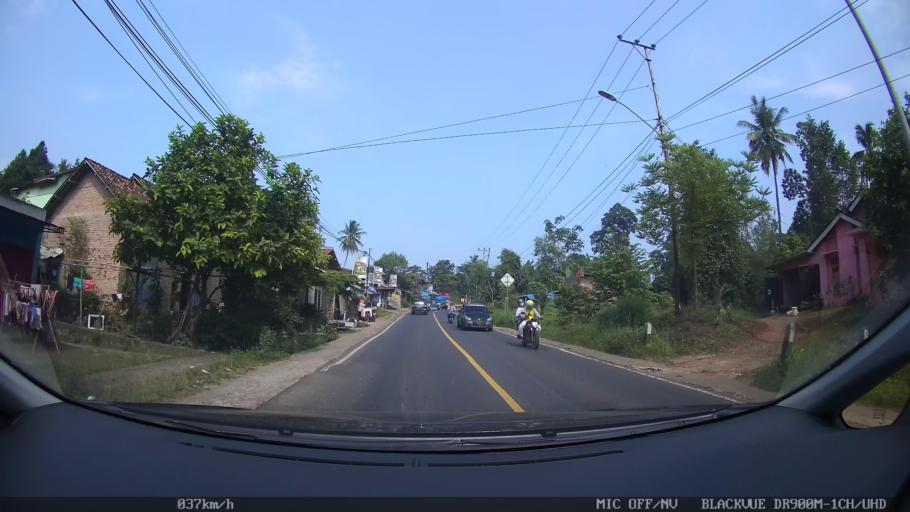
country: ID
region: Lampung
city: Gedongtataan
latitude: -5.3678
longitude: 105.1567
